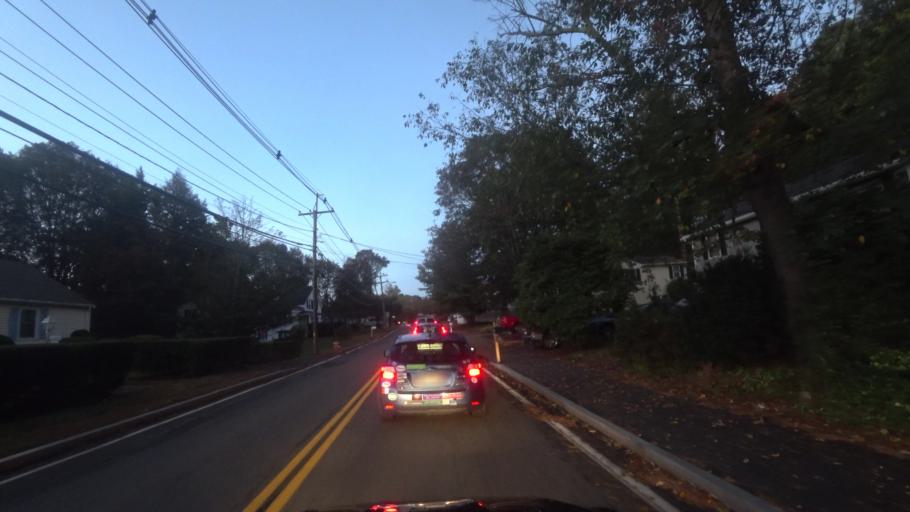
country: US
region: Massachusetts
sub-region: Middlesex County
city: Wakefield
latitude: 42.5016
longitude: -71.0477
